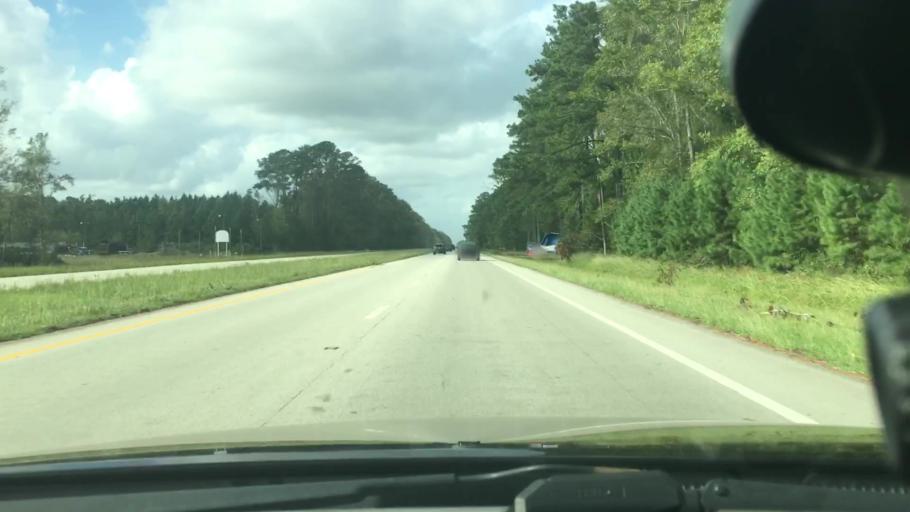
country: US
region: North Carolina
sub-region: Craven County
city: Fairfield Harbour
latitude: 35.0153
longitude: -76.9947
